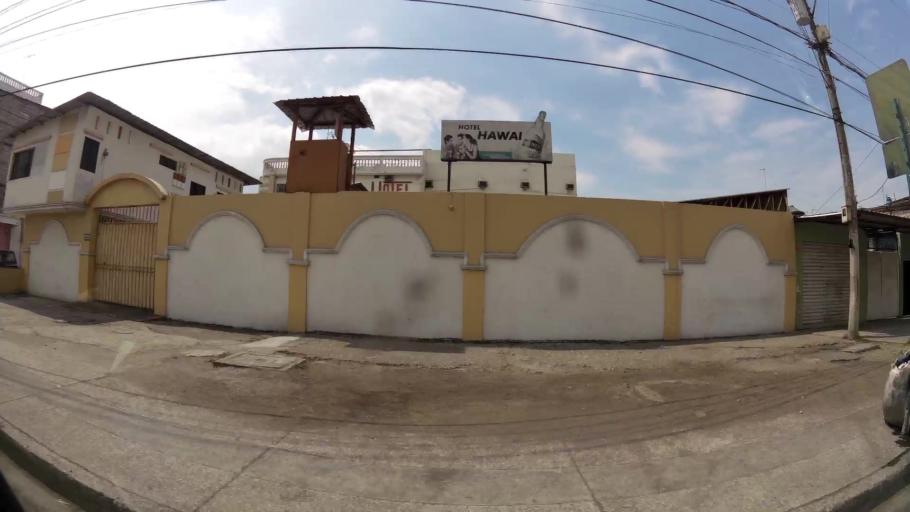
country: EC
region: Guayas
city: Guayaquil
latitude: -2.2435
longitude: -79.8907
